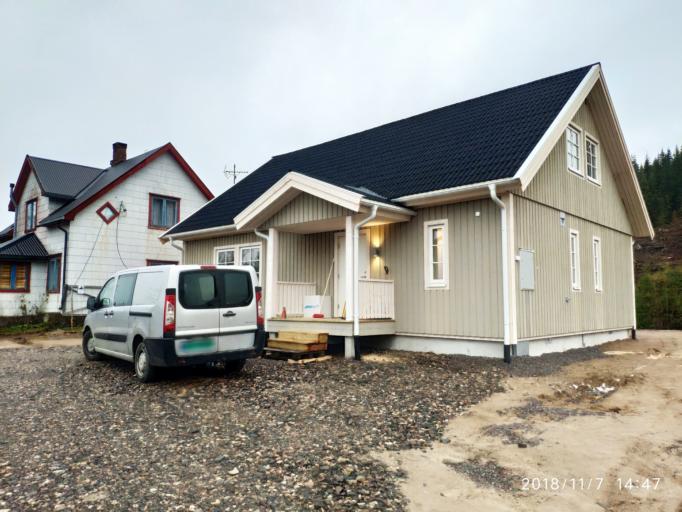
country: NO
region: Hedmark
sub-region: Eidskog
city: Skotterud
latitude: 60.1314
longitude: 12.1715
